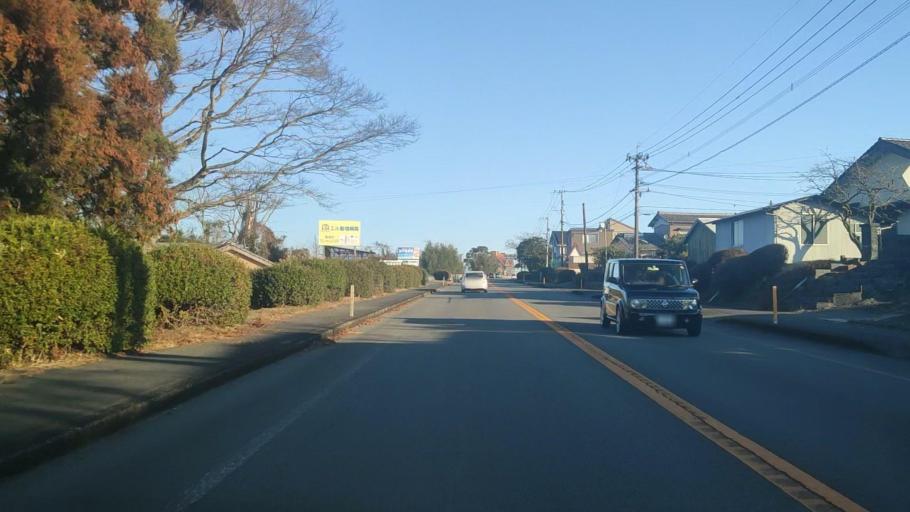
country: JP
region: Miyazaki
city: Takanabe
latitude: 32.1922
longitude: 131.5242
